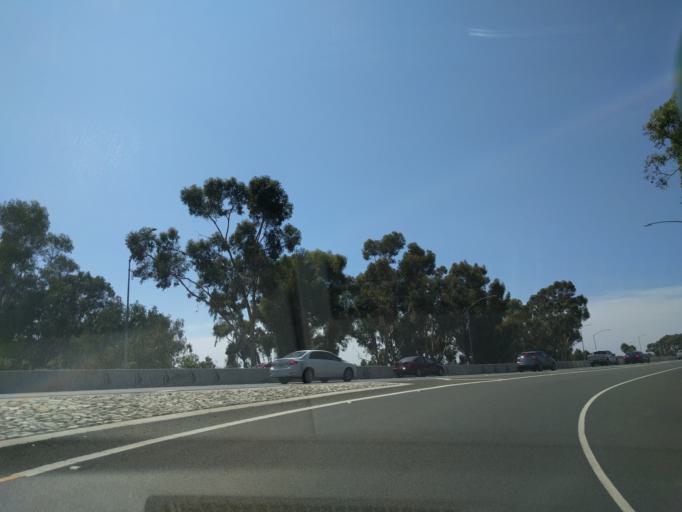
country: US
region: California
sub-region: Orange County
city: Dana Point
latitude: 33.4641
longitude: -117.6779
